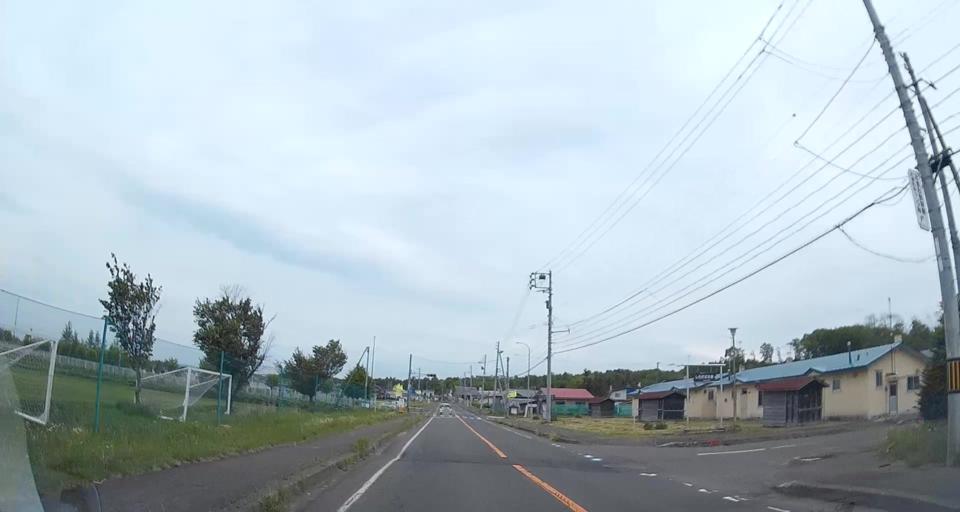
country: JP
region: Hokkaido
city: Chitose
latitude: 42.7698
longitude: 141.8263
